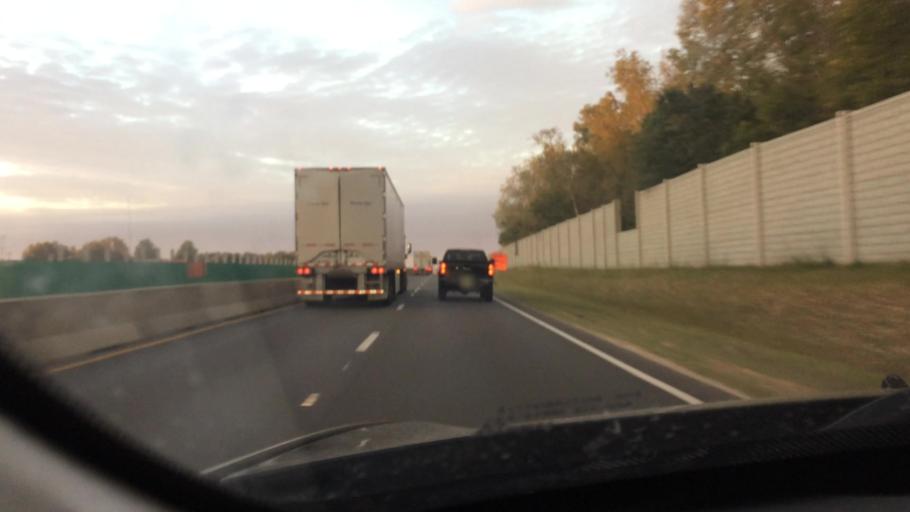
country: US
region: Ohio
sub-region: Hancock County
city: Findlay
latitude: 41.0714
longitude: -83.6625
